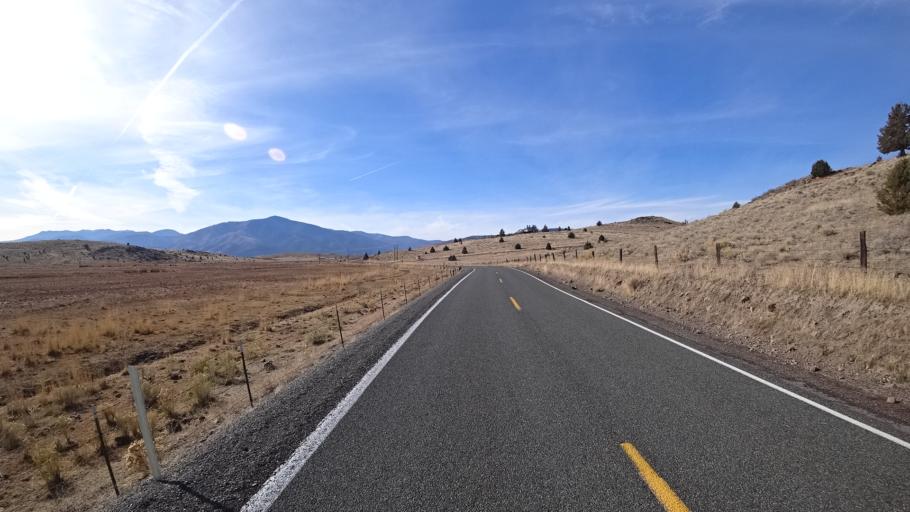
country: US
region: California
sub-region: Siskiyou County
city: Weed
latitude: 41.5403
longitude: -122.5024
